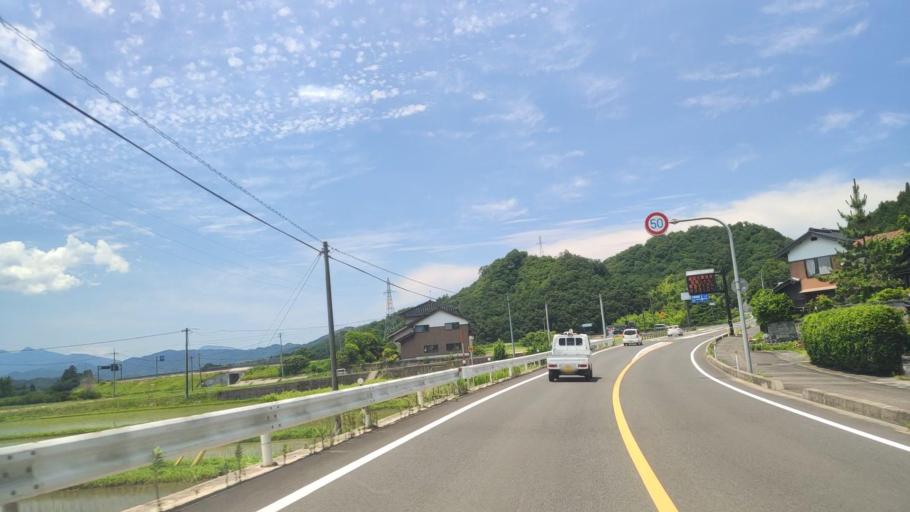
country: JP
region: Tottori
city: Tottori
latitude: 35.3971
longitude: 134.2697
